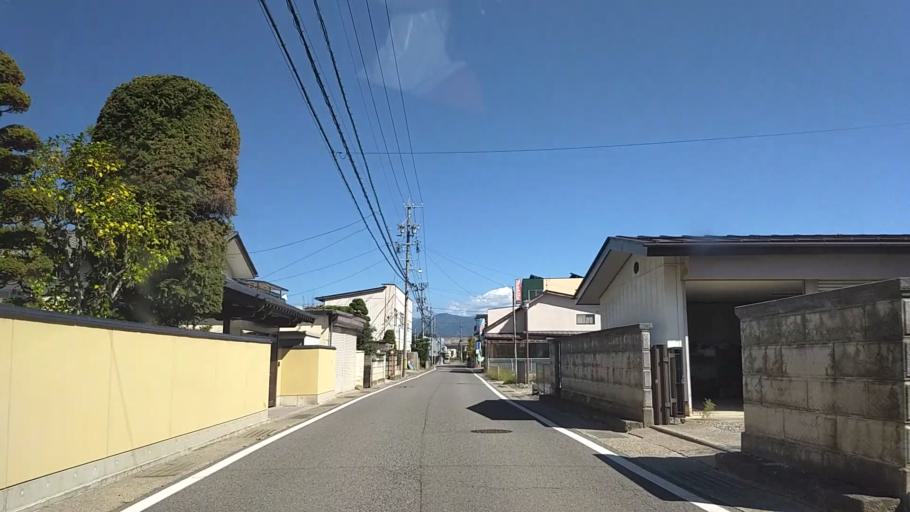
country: JP
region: Nagano
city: Nagano-shi
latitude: 36.6166
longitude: 138.1485
